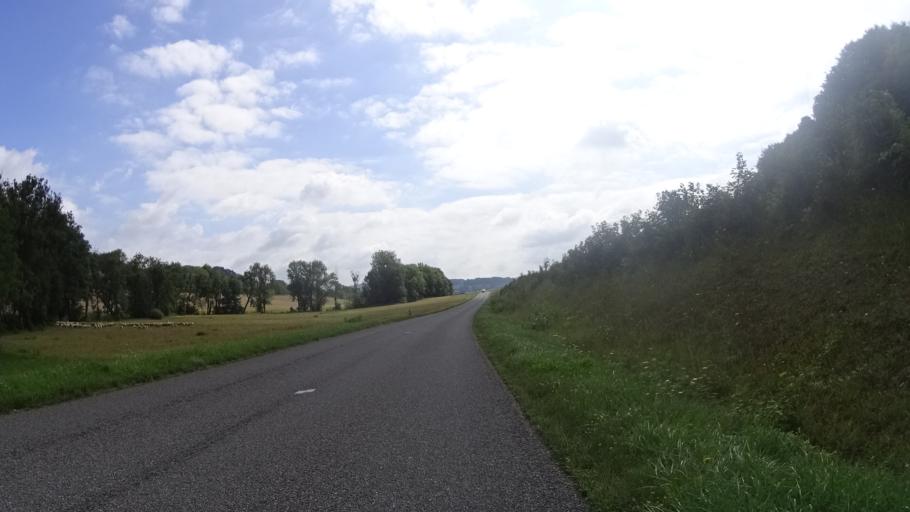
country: FR
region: Lorraine
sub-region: Departement de la Meuse
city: Ligny-en-Barrois
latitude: 48.7172
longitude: 5.3534
